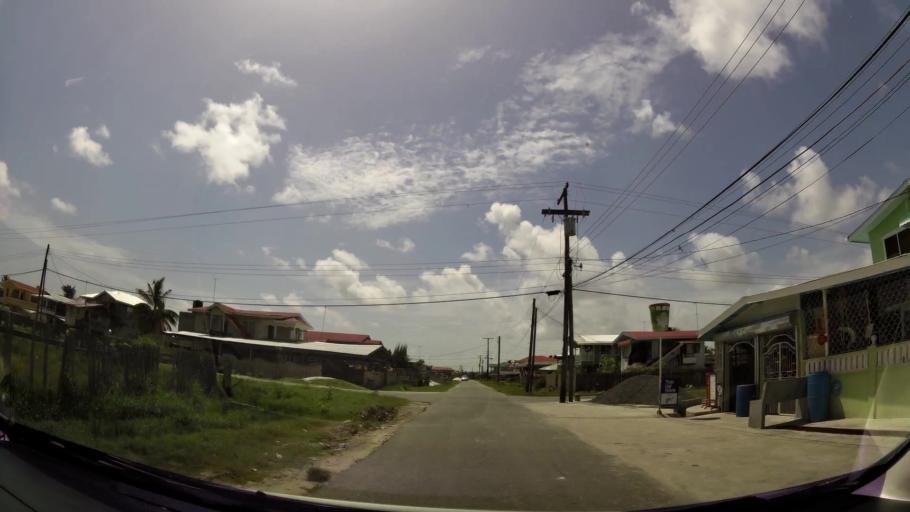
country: GY
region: Demerara-Mahaica
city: Mahaica Village
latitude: 6.7716
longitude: -58.0122
